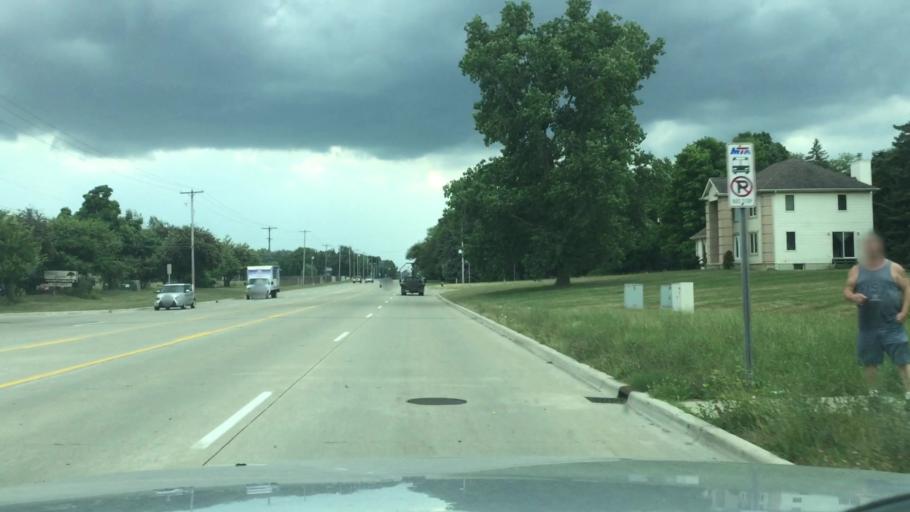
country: US
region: Michigan
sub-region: Genesee County
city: Flushing
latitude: 43.0291
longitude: -83.7736
